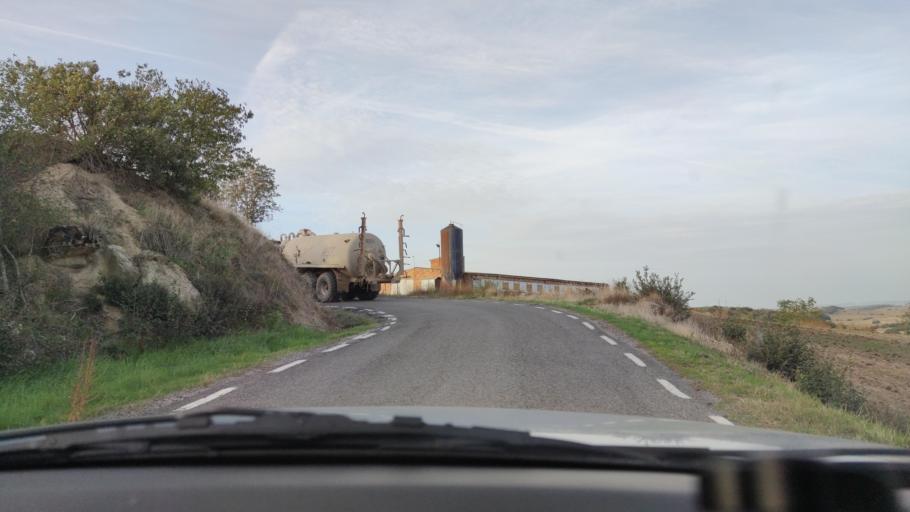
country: ES
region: Catalonia
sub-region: Provincia de Lleida
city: Agramunt
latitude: 41.8383
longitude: 1.0917
